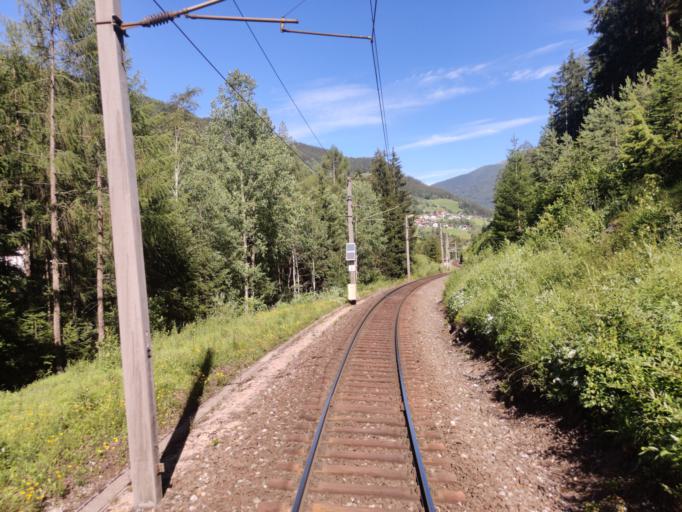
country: AT
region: Tyrol
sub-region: Politischer Bezirk Landeck
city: Strengen
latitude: 47.1273
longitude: 10.4511
